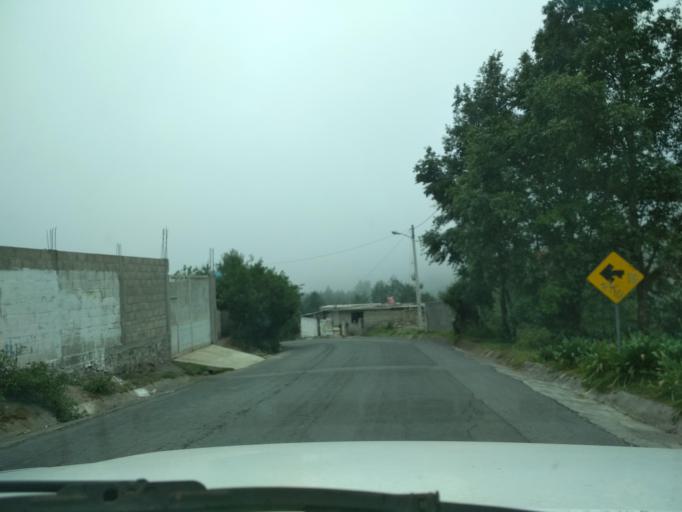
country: MX
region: Veracruz
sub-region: Mariano Escobedo
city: San Isidro el Berro
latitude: 18.9474
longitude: -97.2005
